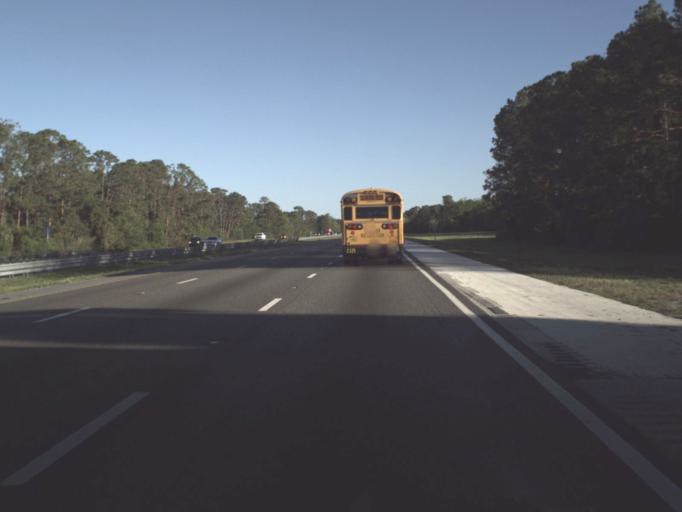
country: US
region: Florida
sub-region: Flagler County
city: Flagler Beach
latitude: 29.4038
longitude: -81.1554
